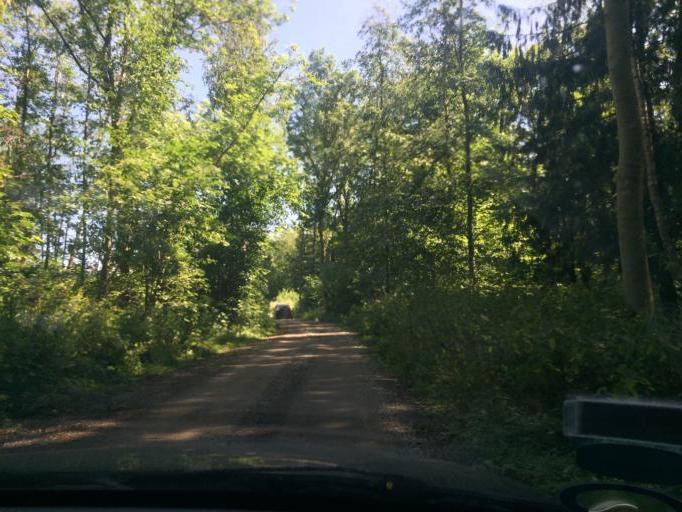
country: DK
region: Zealand
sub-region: Lolland Kommune
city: Maribo
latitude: 54.8184
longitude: 11.4940
